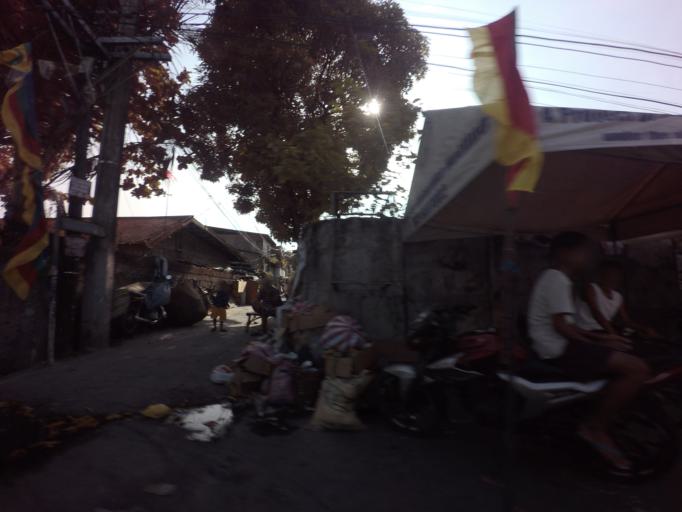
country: PH
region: Calabarzon
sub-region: Province of Rizal
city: Taguig
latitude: 14.4989
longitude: 121.0591
